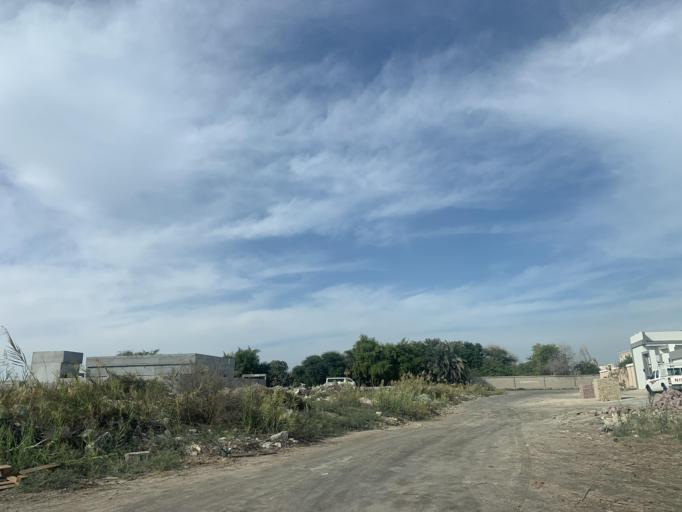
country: BH
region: Central Governorate
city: Madinat Hamad
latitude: 26.1235
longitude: 50.4705
